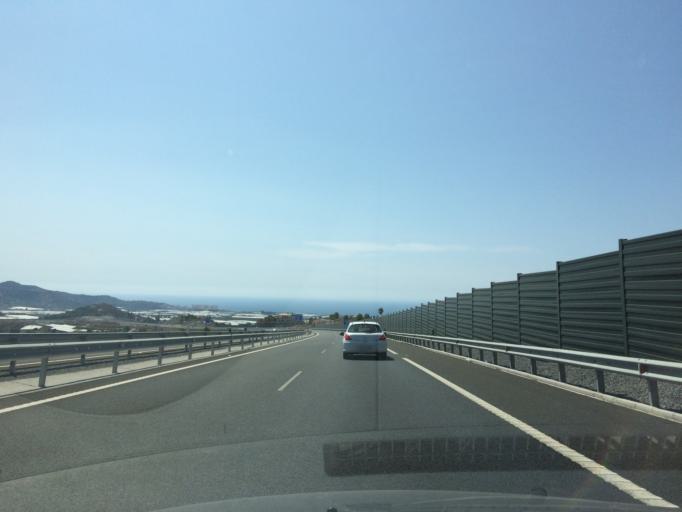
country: ES
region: Andalusia
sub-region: Provincia de Granada
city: Motril
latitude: 36.7506
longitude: -3.4860
